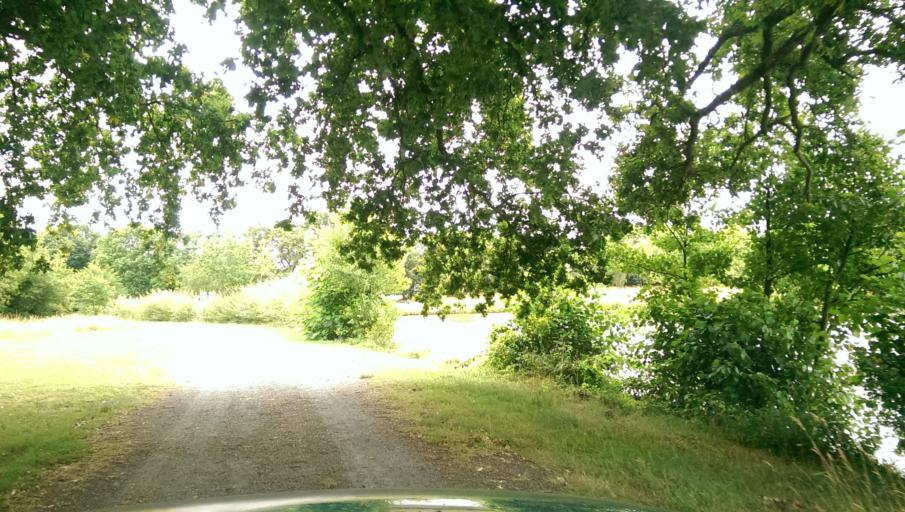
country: FR
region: Pays de la Loire
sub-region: Departement de la Loire-Atlantique
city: La Planche
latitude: 47.0166
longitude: -1.4140
